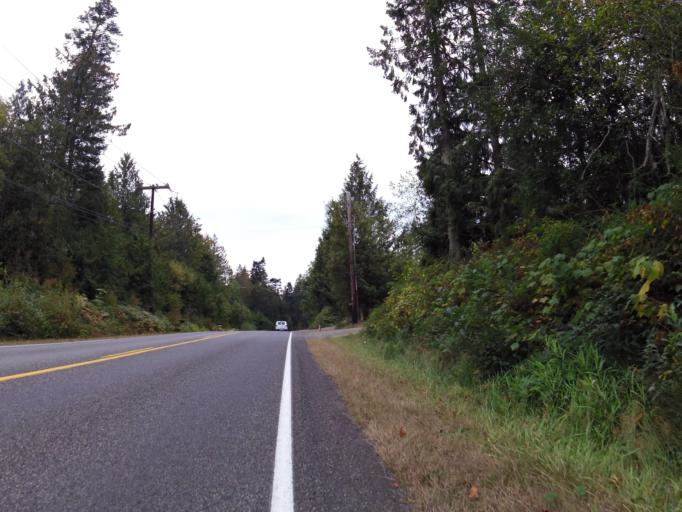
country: US
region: Washington
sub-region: Jefferson County
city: Port Ludlow
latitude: 47.9819
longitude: -122.7149
